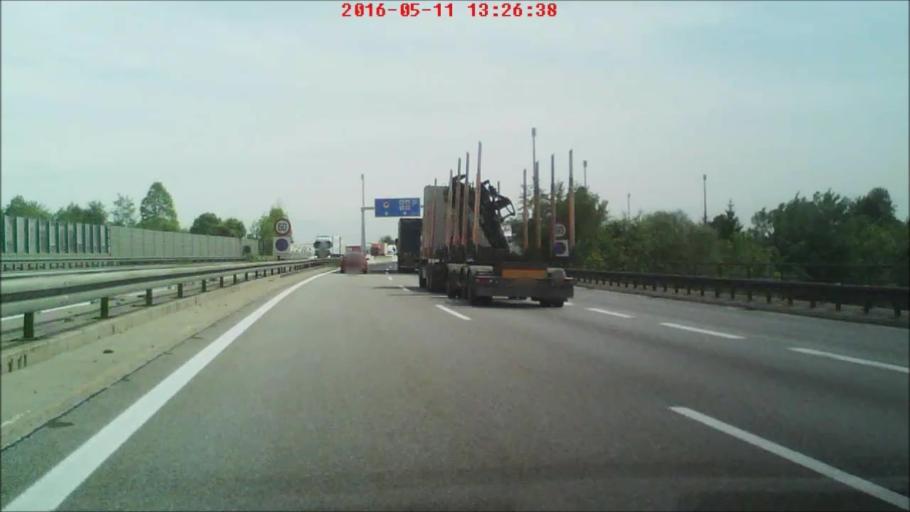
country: AT
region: Upper Austria
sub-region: Politischer Bezirk Scharding
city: Sankt Marienkirchen bei Schaerding
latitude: 48.4104
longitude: 13.4263
